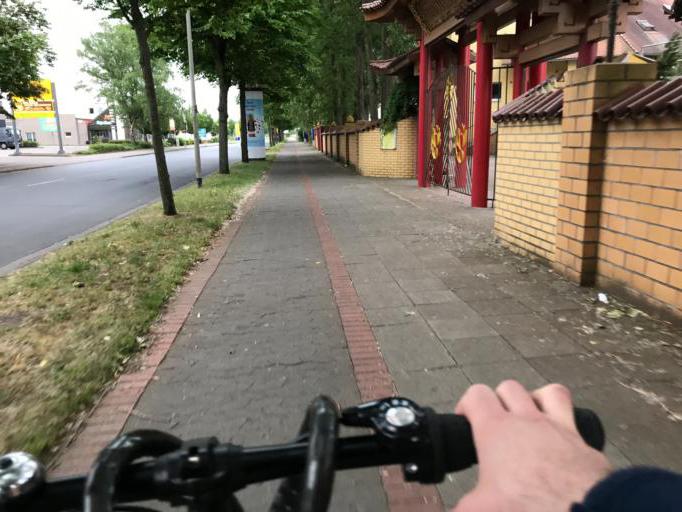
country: DE
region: Lower Saxony
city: Laatzen
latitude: 52.3286
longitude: 9.7907
